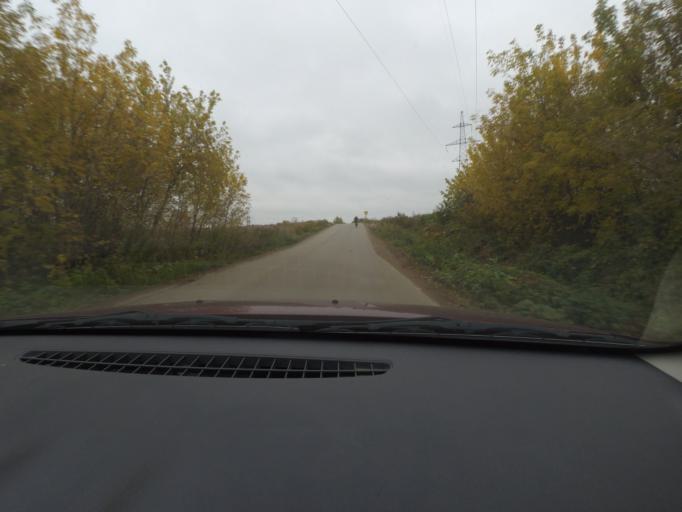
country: RU
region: Nizjnij Novgorod
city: Afonino
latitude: 56.2750
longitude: 44.0562
